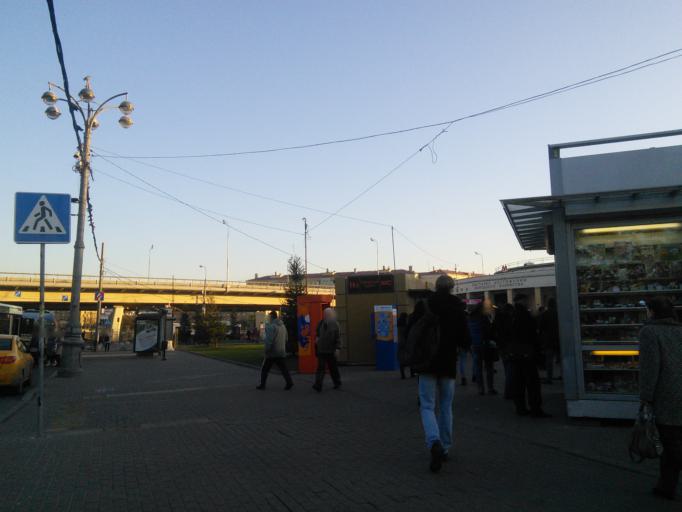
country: RU
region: Moscow
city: Ostankinskiy
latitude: 55.8231
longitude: 37.6415
